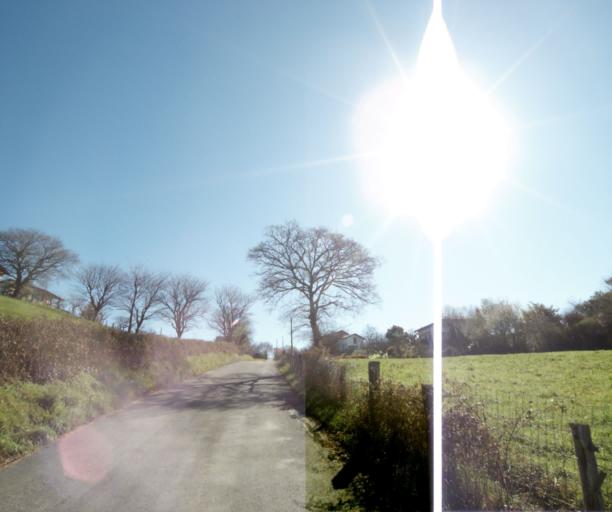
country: FR
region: Aquitaine
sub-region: Departement des Pyrenees-Atlantiques
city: Urrugne
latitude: 43.3458
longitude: -1.6818
